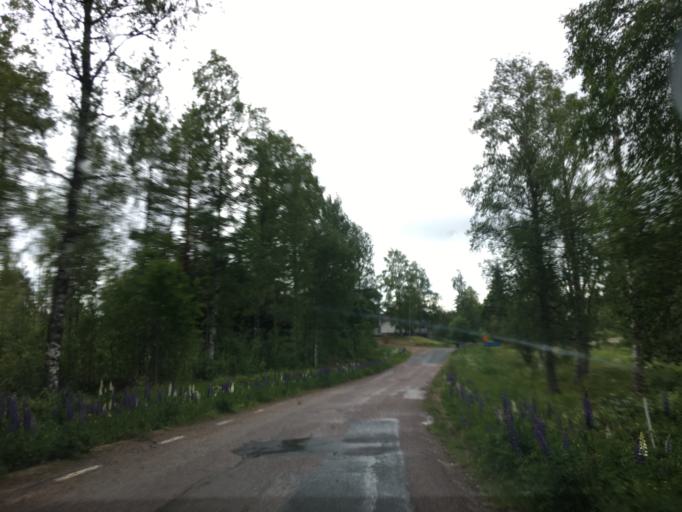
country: SE
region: OErebro
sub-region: Hallefors Kommun
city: Haellefors
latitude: 60.0465
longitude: 14.5065
